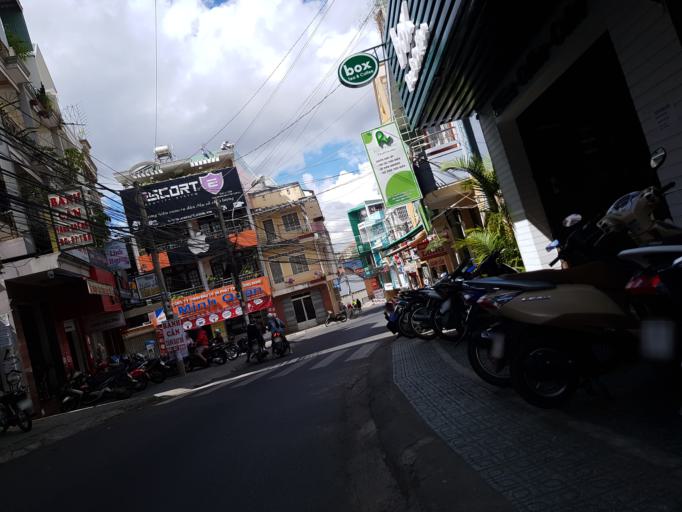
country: VN
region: Lam Dong
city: Da Lat
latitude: 11.9440
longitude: 108.4354
